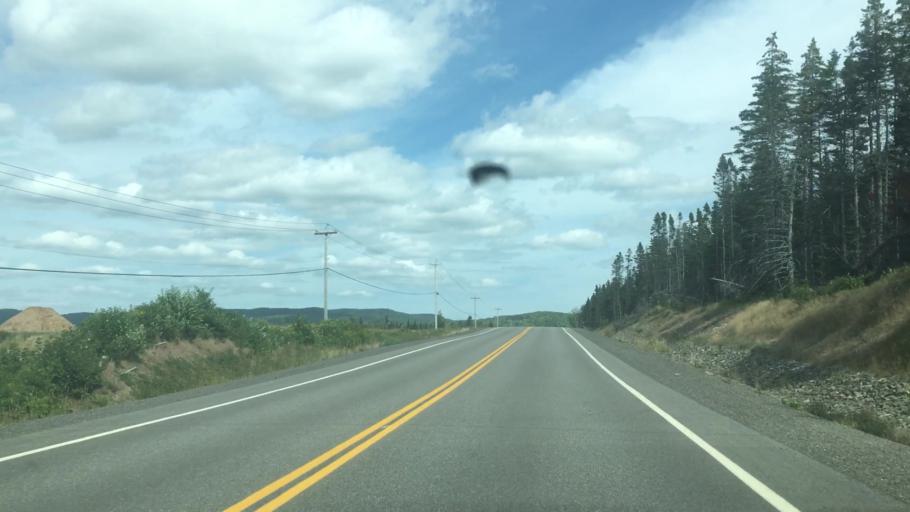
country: CA
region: Nova Scotia
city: Sydney Mines
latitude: 46.3295
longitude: -60.6023
